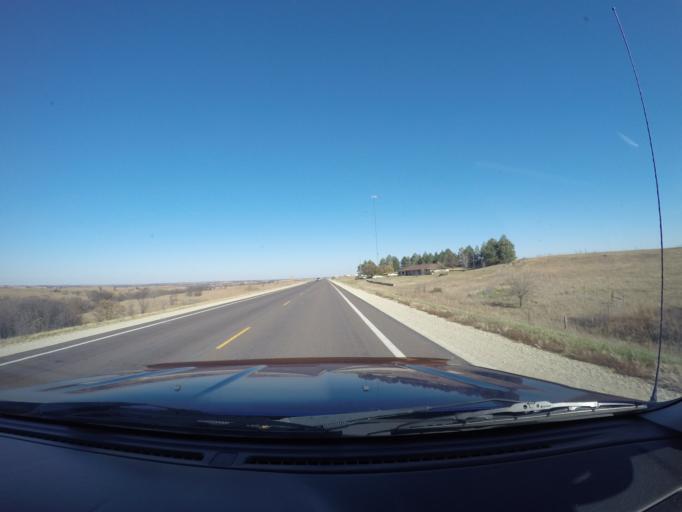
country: US
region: Kansas
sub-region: Marshall County
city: Blue Rapids
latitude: 39.6767
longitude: -96.7508
